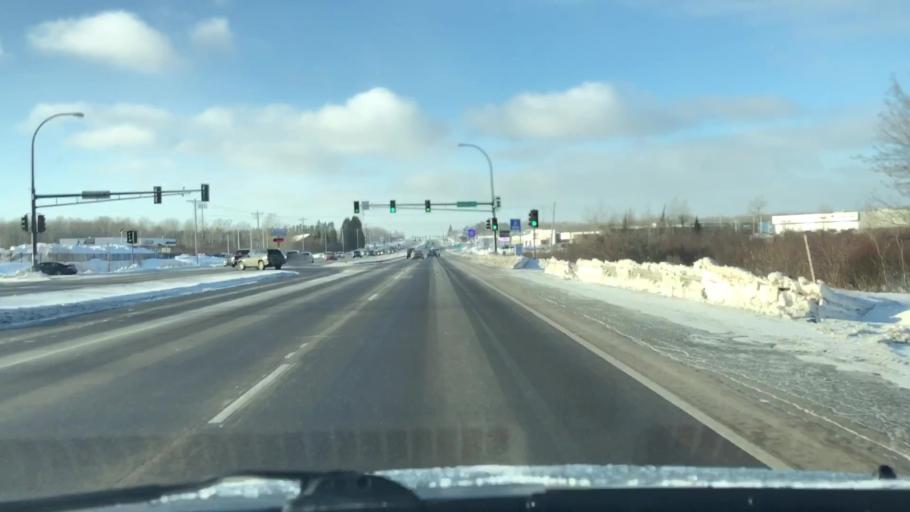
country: US
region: Minnesota
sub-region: Saint Louis County
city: Hermantown
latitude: 46.8187
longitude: -92.1810
